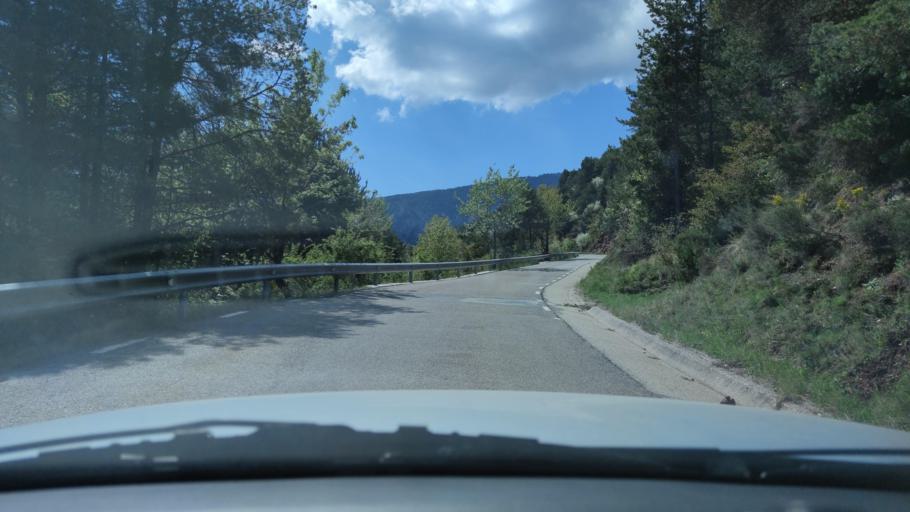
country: ES
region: Catalonia
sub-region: Provincia de Lleida
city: Coll de Nargo
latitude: 42.3065
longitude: 1.2821
